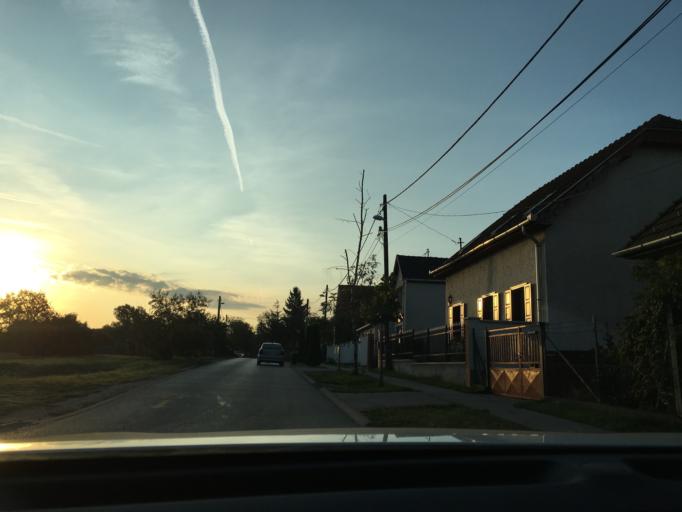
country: HU
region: Budapest
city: Budapest XVII. keruelet
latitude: 47.4754
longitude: 19.2599
